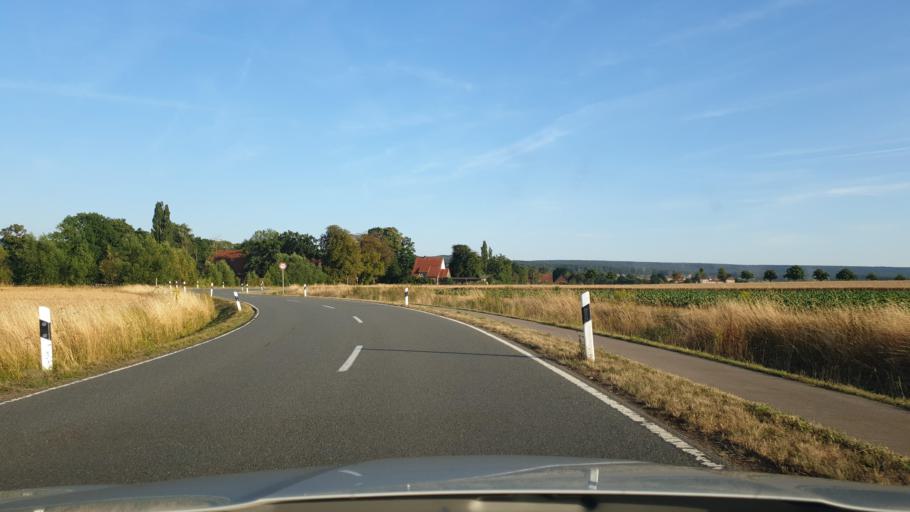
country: DE
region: Lower Saxony
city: Heuerssen
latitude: 52.3206
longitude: 9.2503
